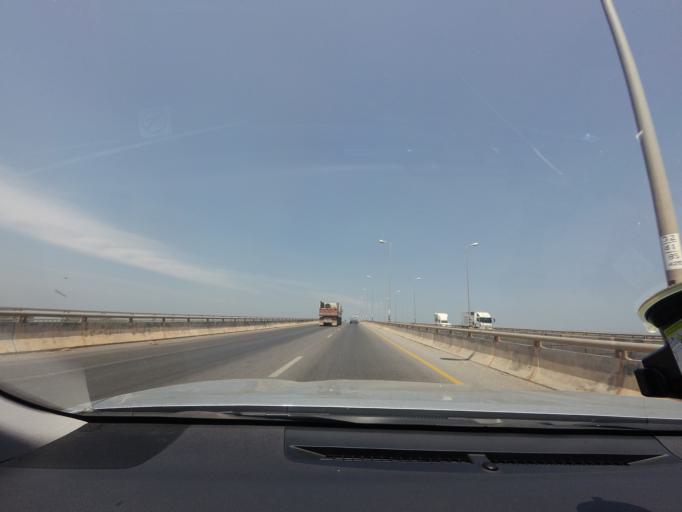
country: TH
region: Surat Thani
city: Surat Thani
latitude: 9.1727
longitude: 99.3598
